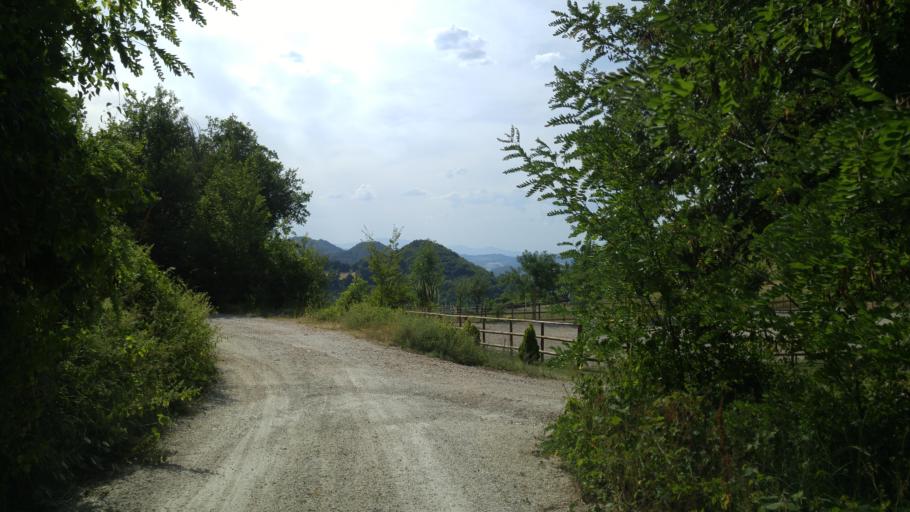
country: IT
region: The Marches
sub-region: Provincia di Pesaro e Urbino
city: Canavaccio
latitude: 43.6696
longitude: 12.7294
